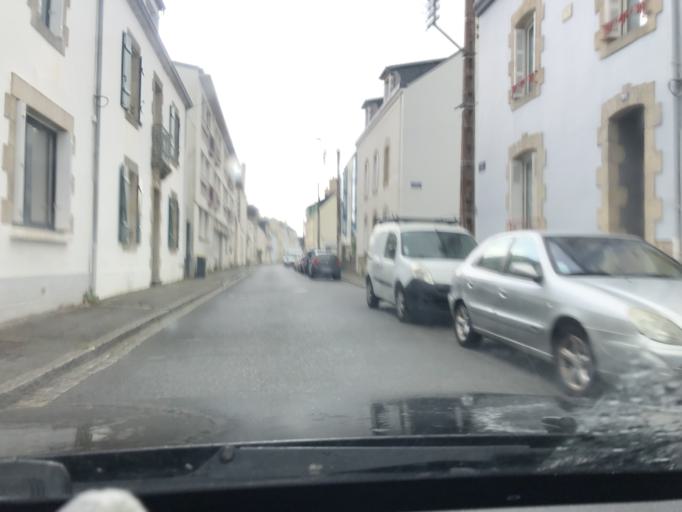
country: FR
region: Brittany
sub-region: Departement du Morbihan
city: Lorient
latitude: 47.7429
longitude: -3.3771
